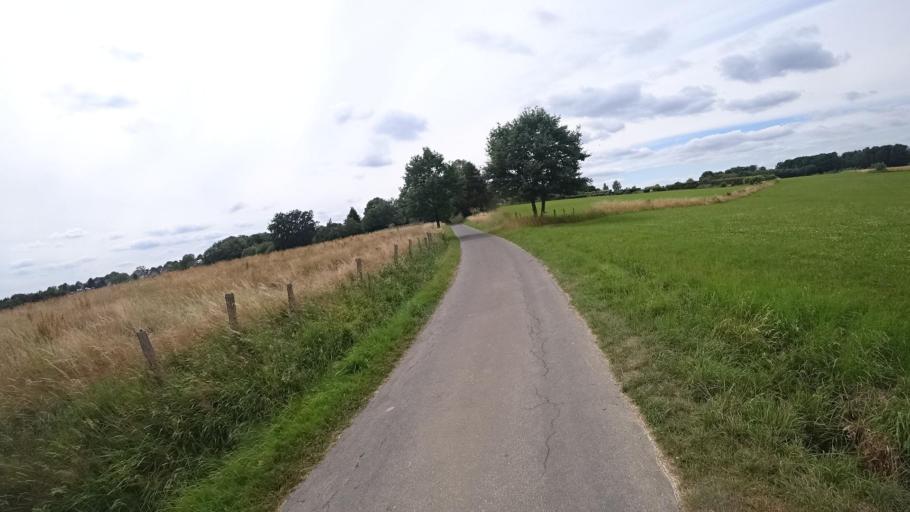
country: DE
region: Rheinland-Pfalz
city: Ziegenhain
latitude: 50.6781
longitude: 7.5318
